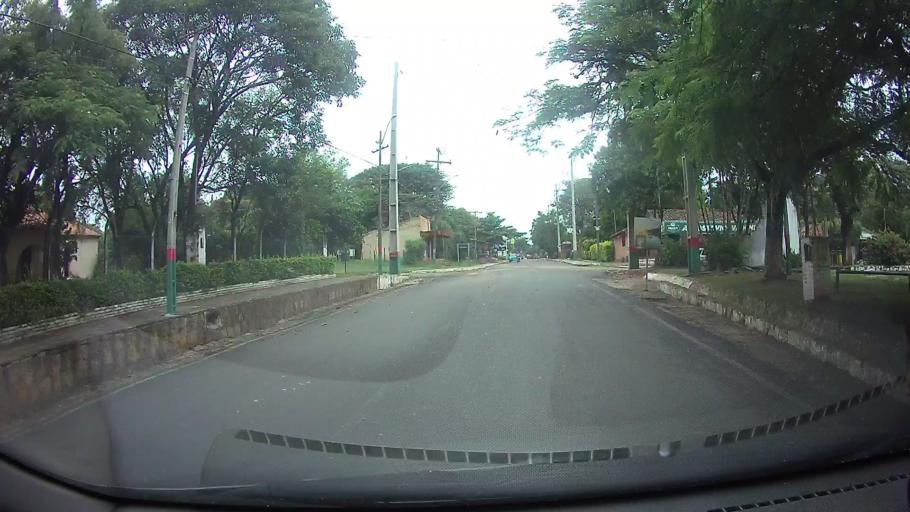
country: PY
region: Cordillera
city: Altos
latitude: -25.2636
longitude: -57.2479
